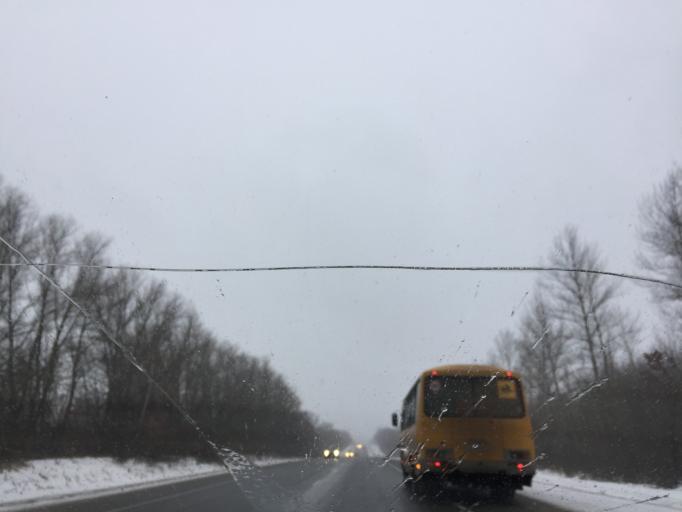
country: RU
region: Tula
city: Plavsk
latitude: 53.7399
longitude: 37.3165
